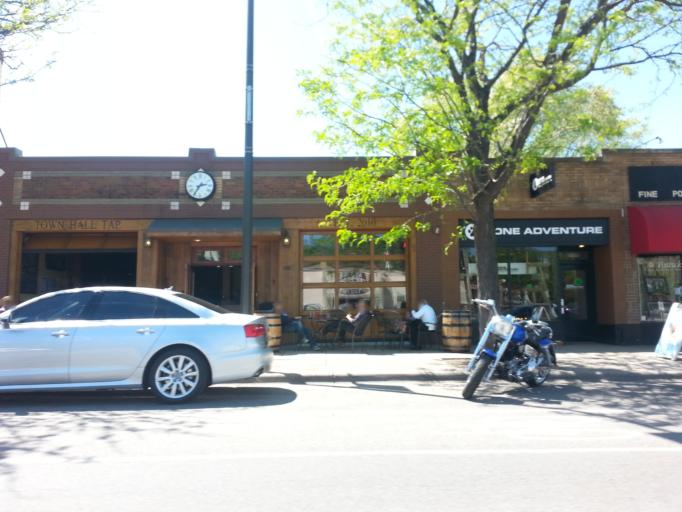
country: US
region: Minnesota
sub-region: Hennepin County
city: Richfield
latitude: 44.9158
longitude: -93.2627
